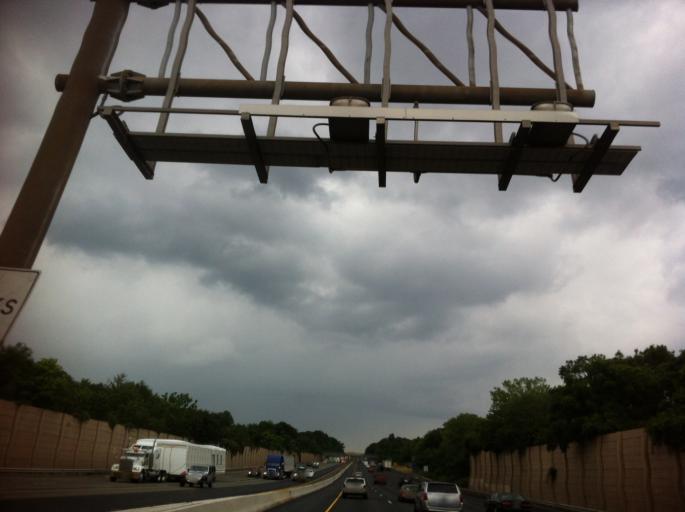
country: US
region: New Jersey
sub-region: Morris County
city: Mountain Lakes
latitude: 40.8872
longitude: -74.4722
